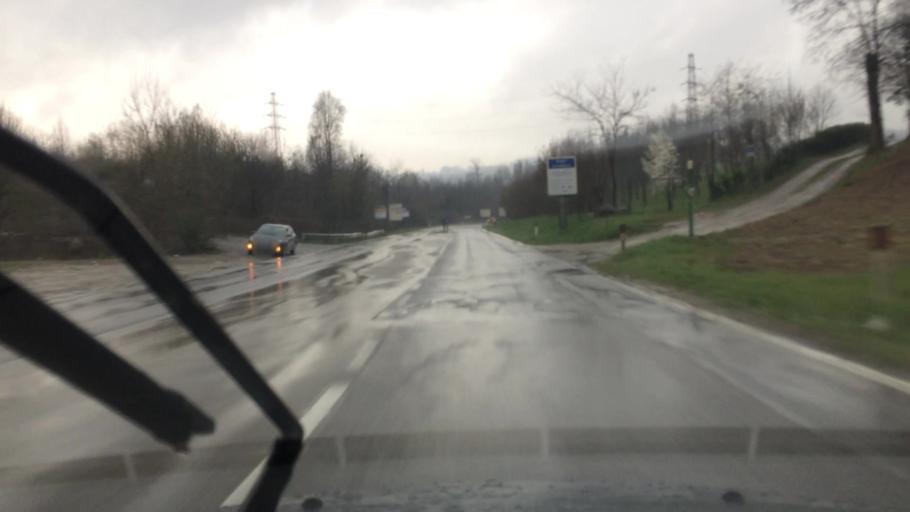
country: IT
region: Lombardy
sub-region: Provincia di Como
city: Montesolaro
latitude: 45.7227
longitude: 9.1043
